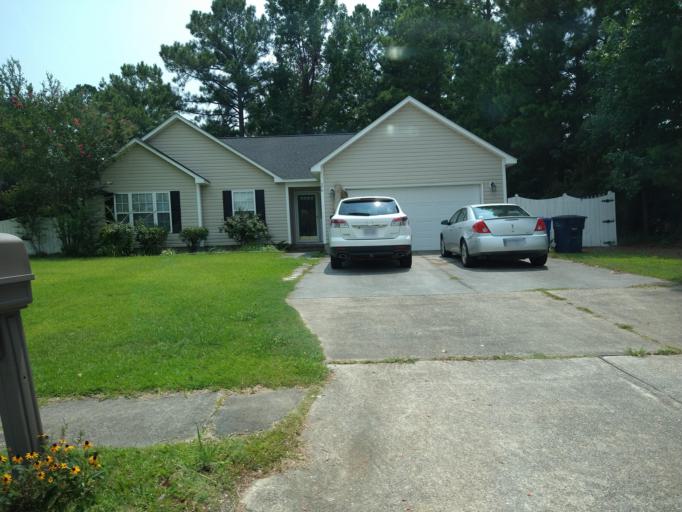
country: US
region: North Carolina
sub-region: Onslow County
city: Pumpkin Center
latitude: 34.7607
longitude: -77.3763
